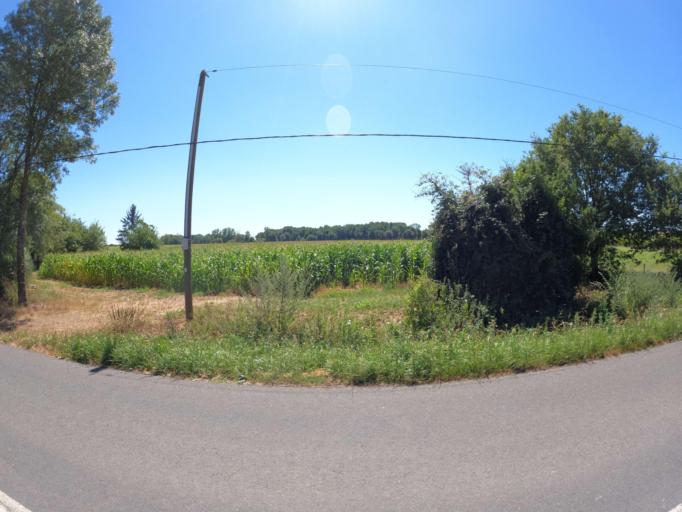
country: FR
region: Pays de la Loire
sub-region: Departement de la Vendee
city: Saint-Philbert-de-Bouaine
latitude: 46.9734
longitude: -1.5579
